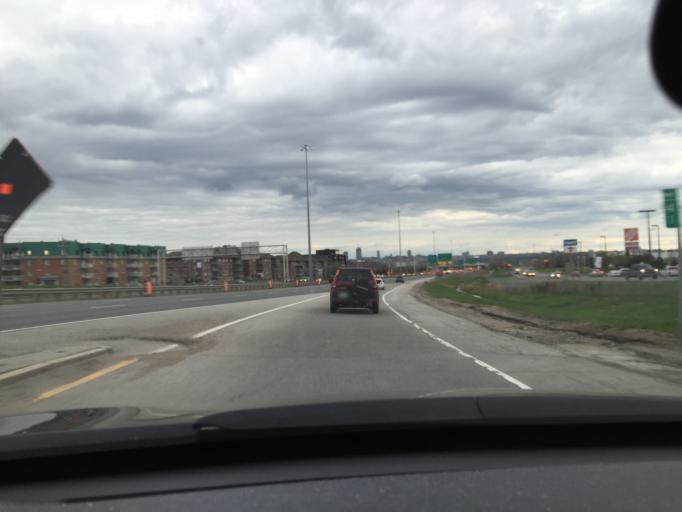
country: CA
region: Quebec
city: Quebec
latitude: 46.8446
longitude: -71.2717
